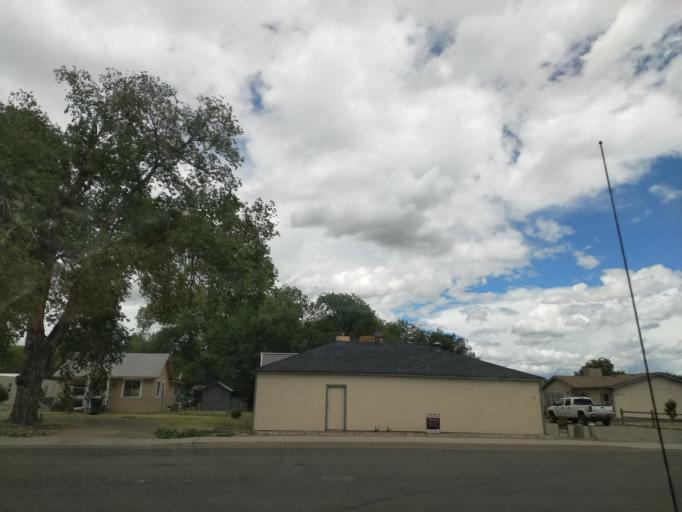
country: US
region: Colorado
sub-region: Mesa County
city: Orchard Mesa
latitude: 39.0483
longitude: -108.5523
